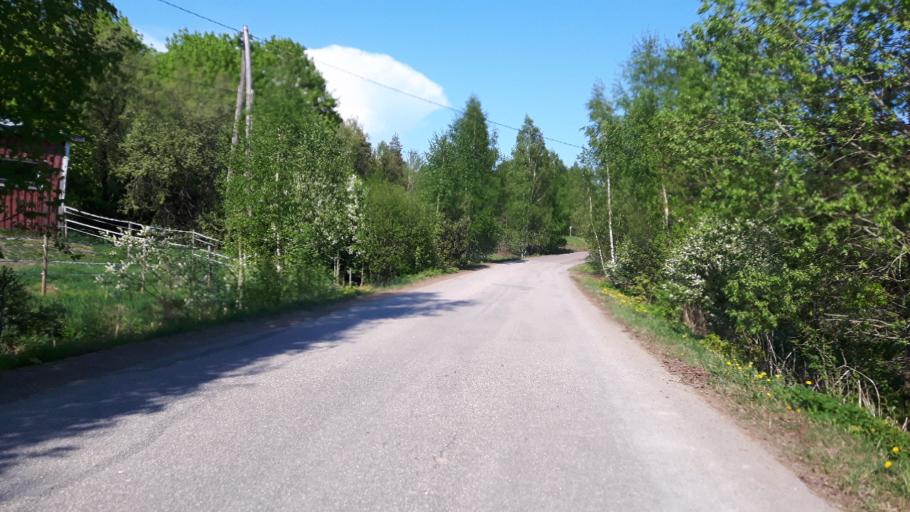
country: FI
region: Kymenlaakso
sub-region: Kotka-Hamina
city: Broby
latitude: 60.4964
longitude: 26.7756
